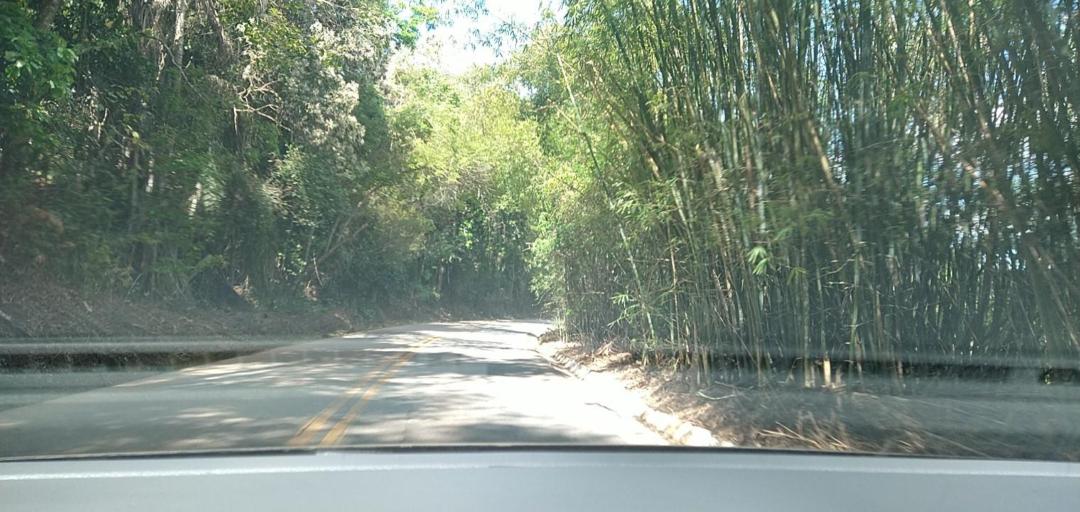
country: BR
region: Minas Gerais
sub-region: Rio Piracicaba
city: Rio Piracicaba
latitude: -19.9507
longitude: -43.1727
